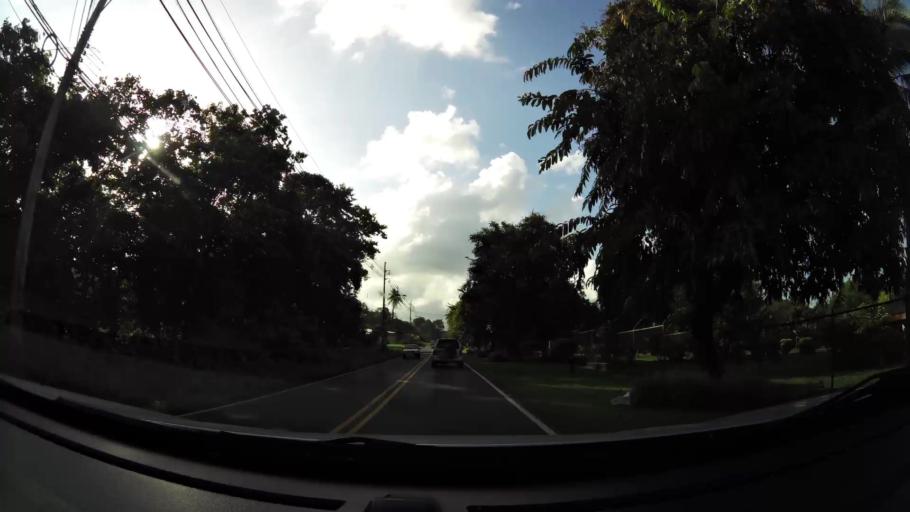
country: CR
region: Limon
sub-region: Canton de Siquirres
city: Siquirres
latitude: 10.0960
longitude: -83.5192
